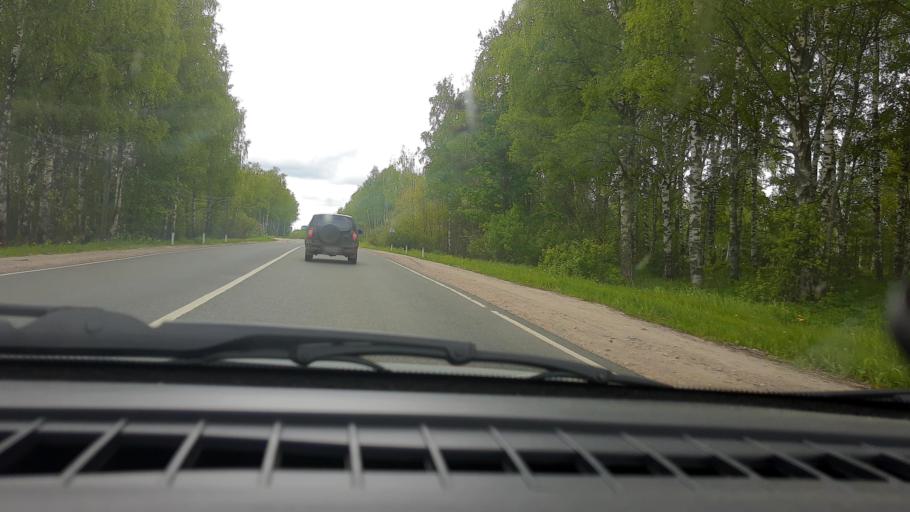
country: RU
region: Nizjnij Novgorod
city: Krasnyye Baki
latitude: 57.0610
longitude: 45.1372
